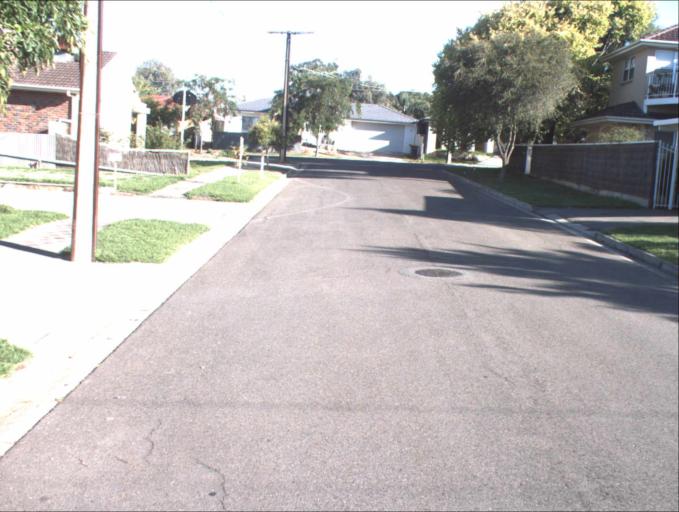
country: AU
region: South Australia
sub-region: Port Adelaide Enfield
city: Klemzig
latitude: -34.8724
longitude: 138.6512
